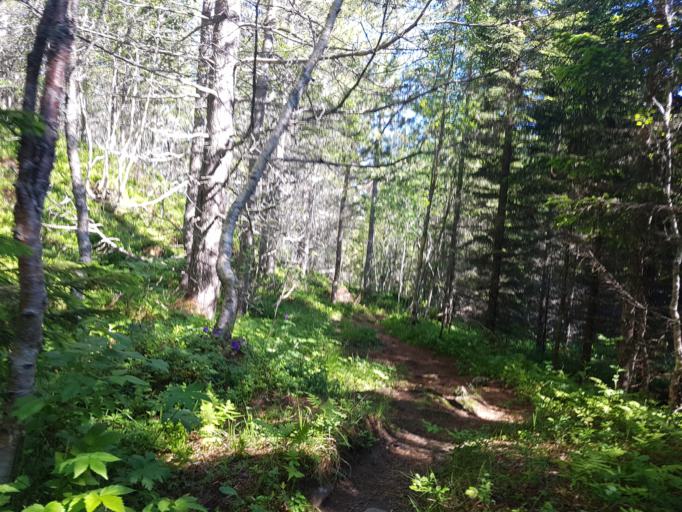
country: NO
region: Sor-Trondelag
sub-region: Trondheim
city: Trondheim
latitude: 63.4394
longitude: 10.2655
